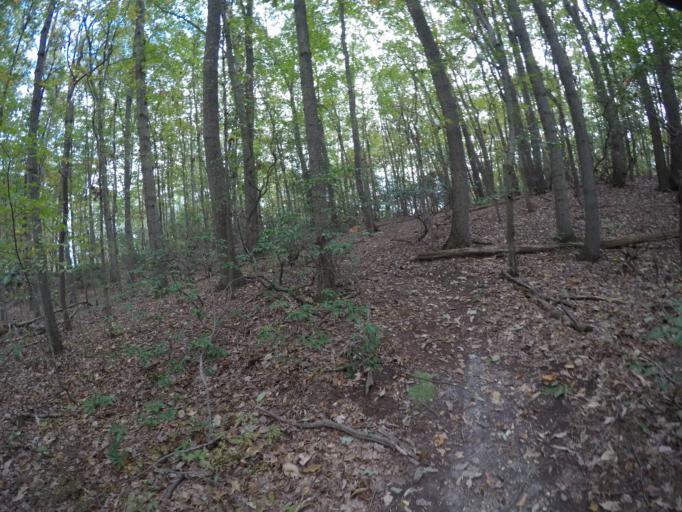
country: US
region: Maryland
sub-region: Harford County
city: Riverside
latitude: 39.4542
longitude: -76.2673
